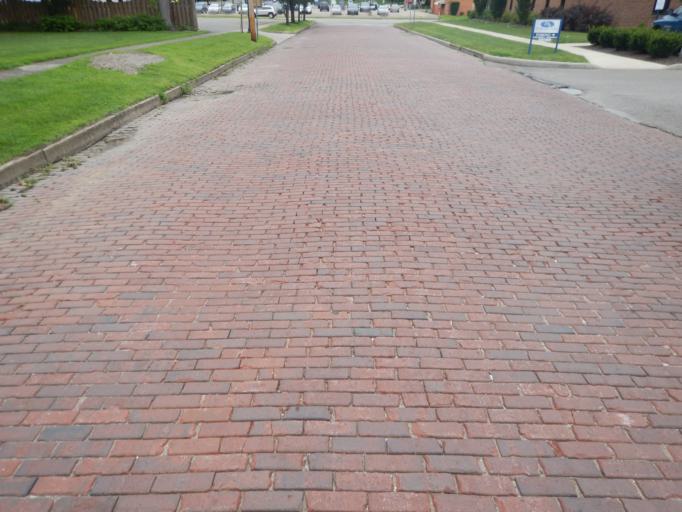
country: US
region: Ohio
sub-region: Muskingum County
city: Zanesville
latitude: 39.9524
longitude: -82.0131
